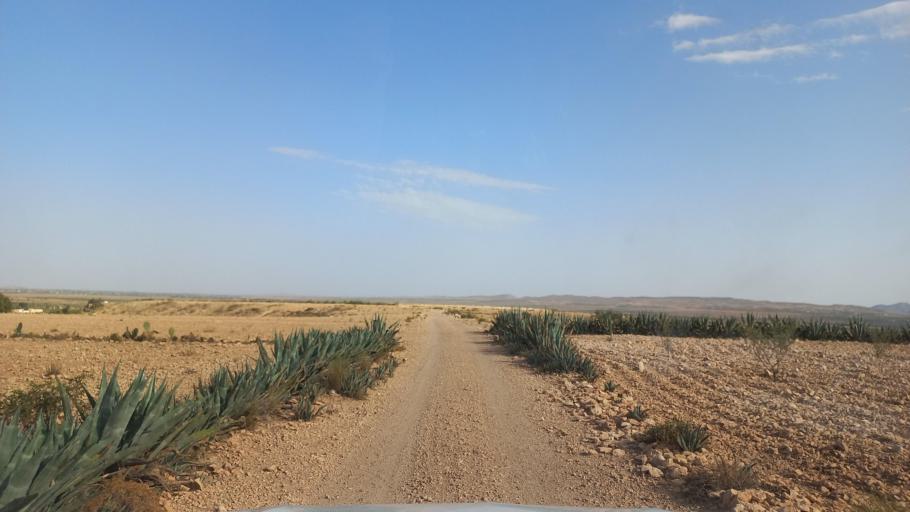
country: TN
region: Al Qasrayn
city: Kasserine
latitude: 35.2595
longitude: 8.9291
